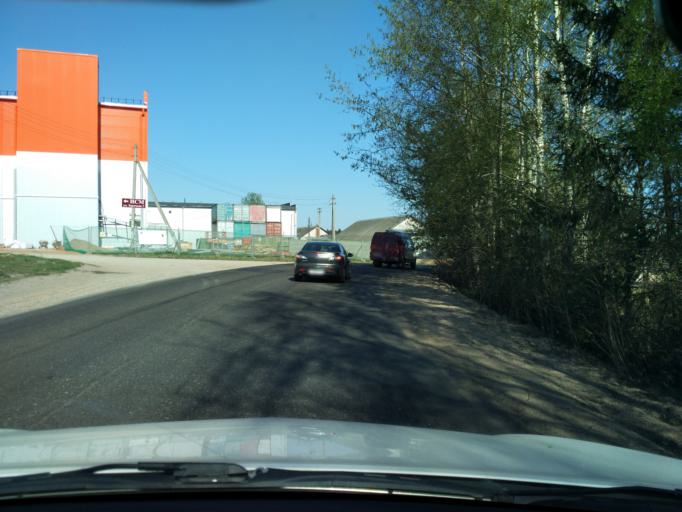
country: BY
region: Minsk
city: Korolev Stan
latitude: 53.9923
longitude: 27.7942
